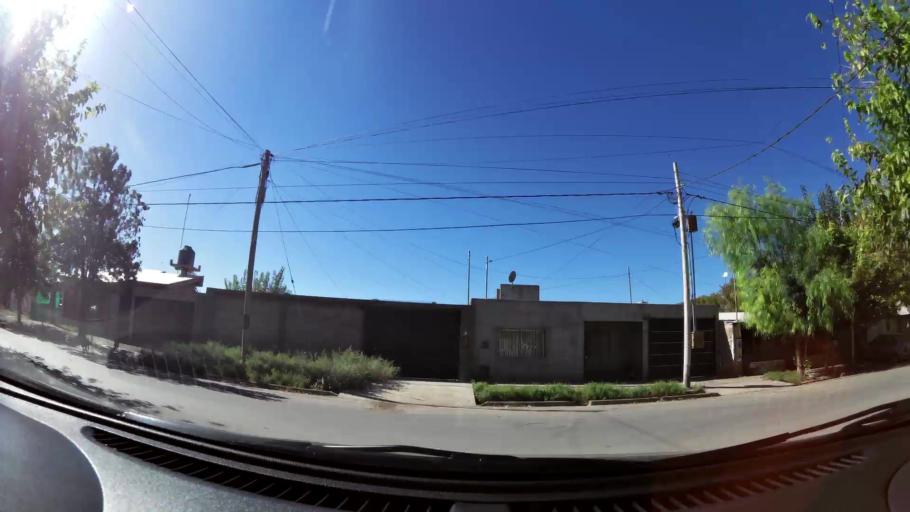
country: AR
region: Mendoza
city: Las Heras
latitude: -32.8395
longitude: -68.8262
